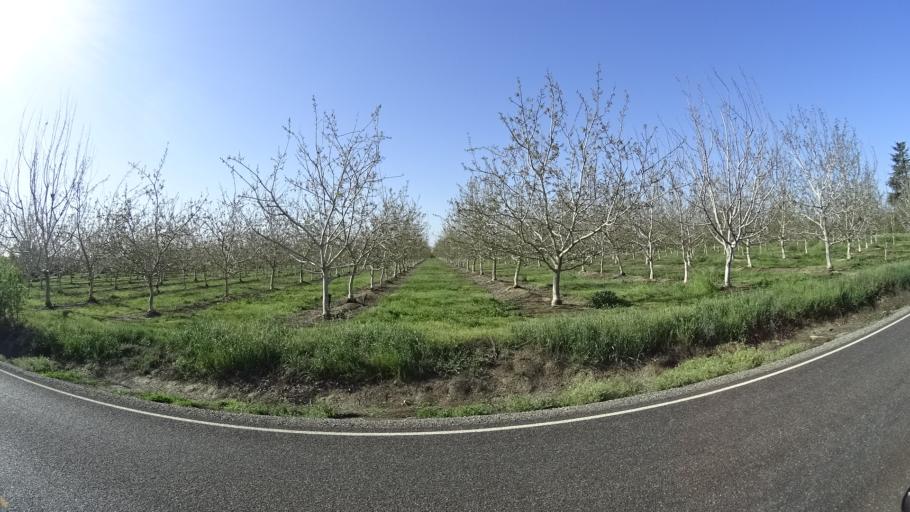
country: US
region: California
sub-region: Glenn County
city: Hamilton City
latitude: 39.7092
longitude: -122.0601
